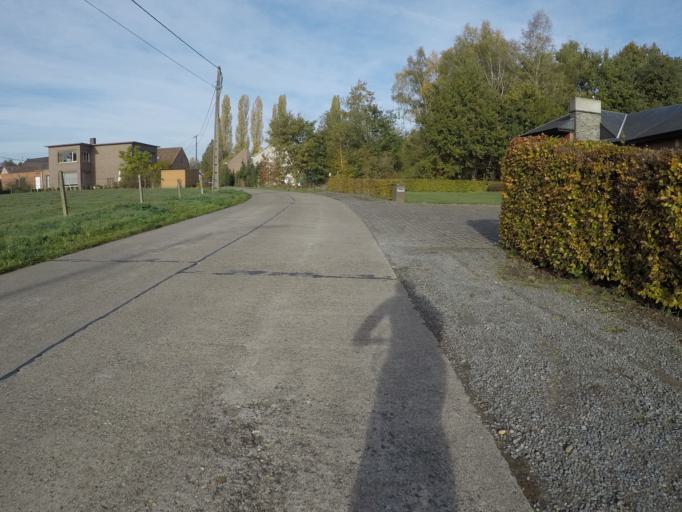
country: BE
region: Flanders
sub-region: Provincie Vlaams-Brabant
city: Begijnendijk
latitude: 51.0077
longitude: 4.7707
